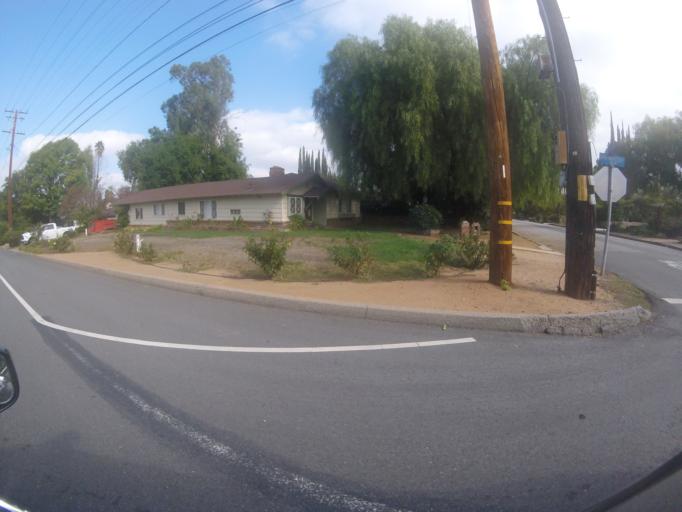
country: US
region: California
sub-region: San Bernardino County
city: Redlands
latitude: 34.0354
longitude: -117.1879
